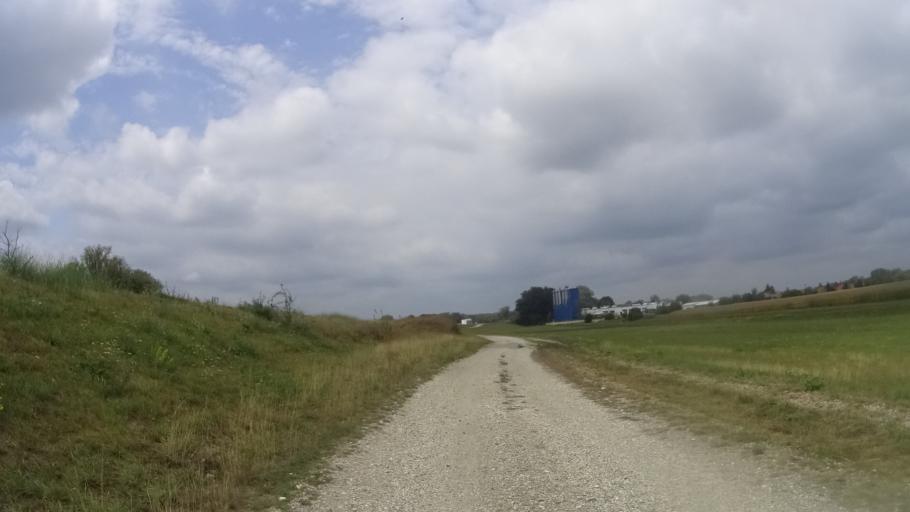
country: HU
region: Gyor-Moson-Sopron
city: Bony
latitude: 47.7437
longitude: 17.8840
